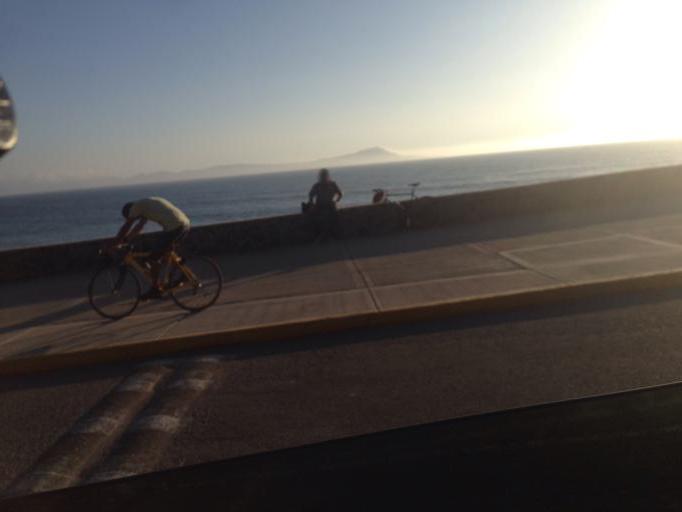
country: MX
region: Baja California
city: Ensenada
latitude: 31.8607
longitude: -116.6398
